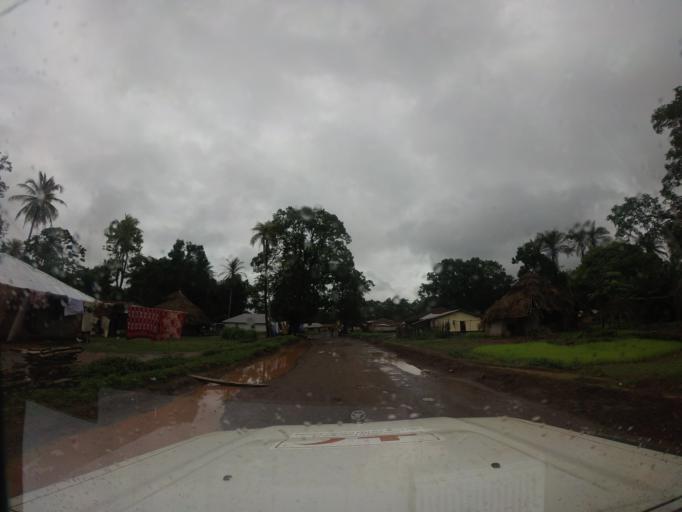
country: SL
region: Northern Province
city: Kambia
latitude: 9.1378
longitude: -12.8804
